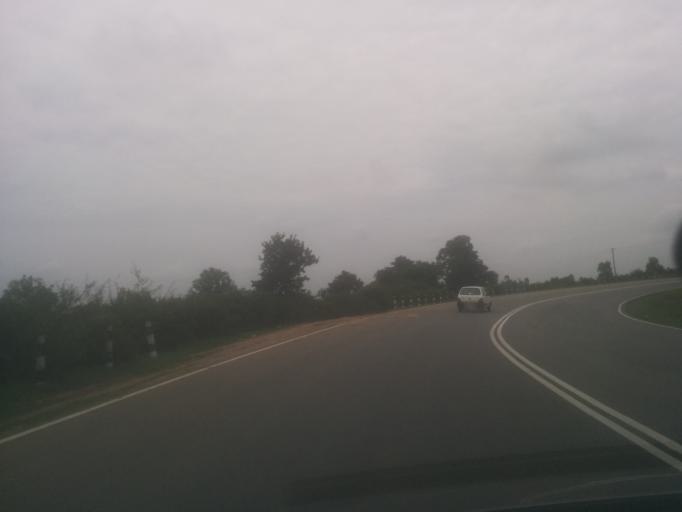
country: IN
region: Karnataka
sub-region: Hassan
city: Belur
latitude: 13.1634
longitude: 75.8989
